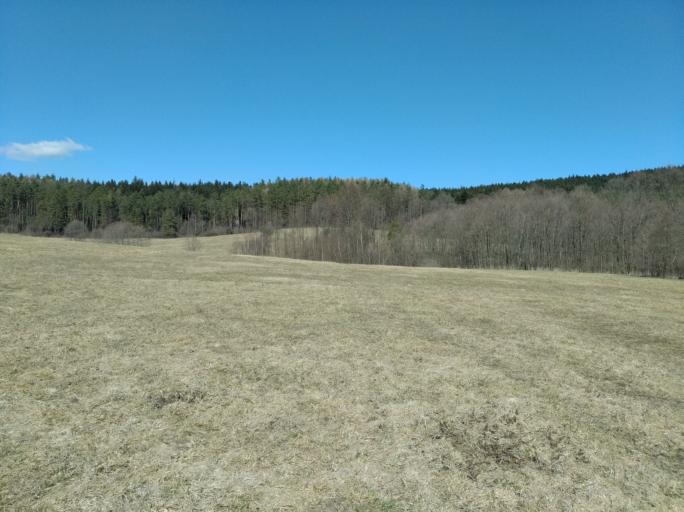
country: PL
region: Subcarpathian Voivodeship
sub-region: Powiat krosnienski
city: Korczyna
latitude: 49.7820
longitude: 21.8372
